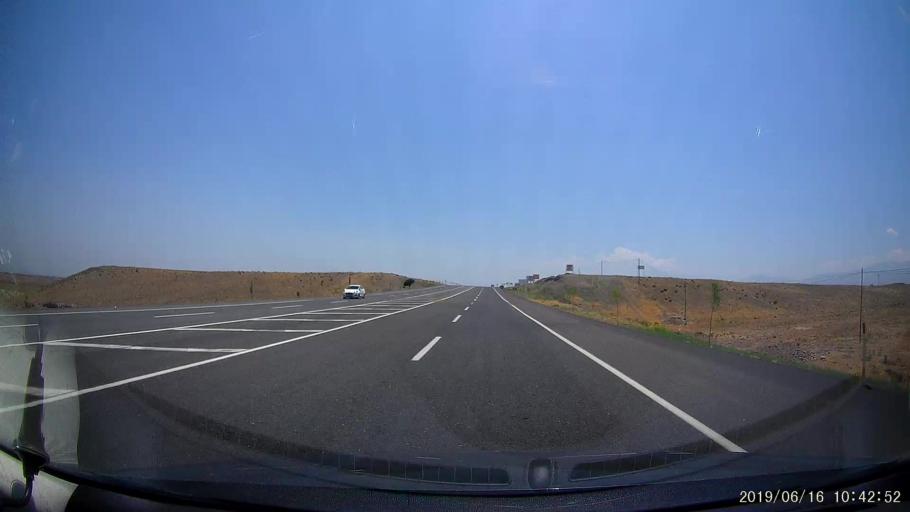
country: AM
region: Armavir
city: Shenavan
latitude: 40.0390
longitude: 43.8157
